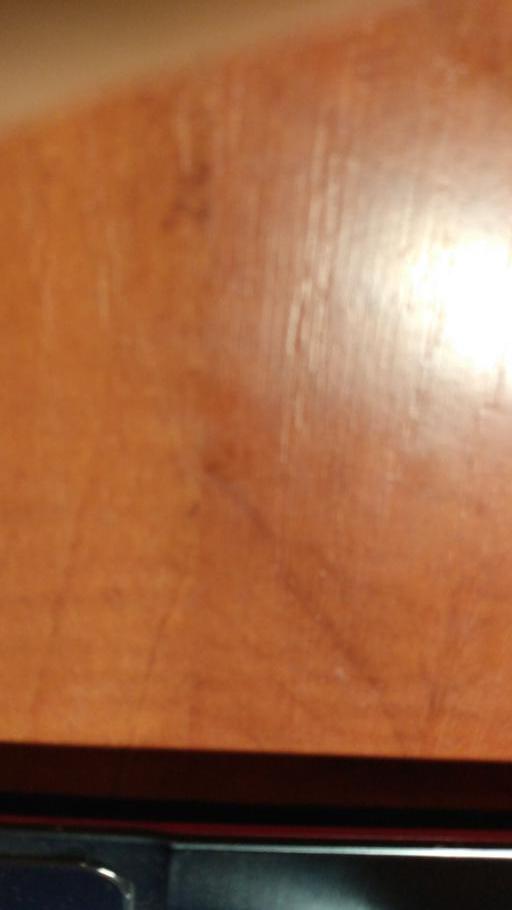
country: RU
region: Novgorod
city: Marevo
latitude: 57.3418
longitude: 31.9735
